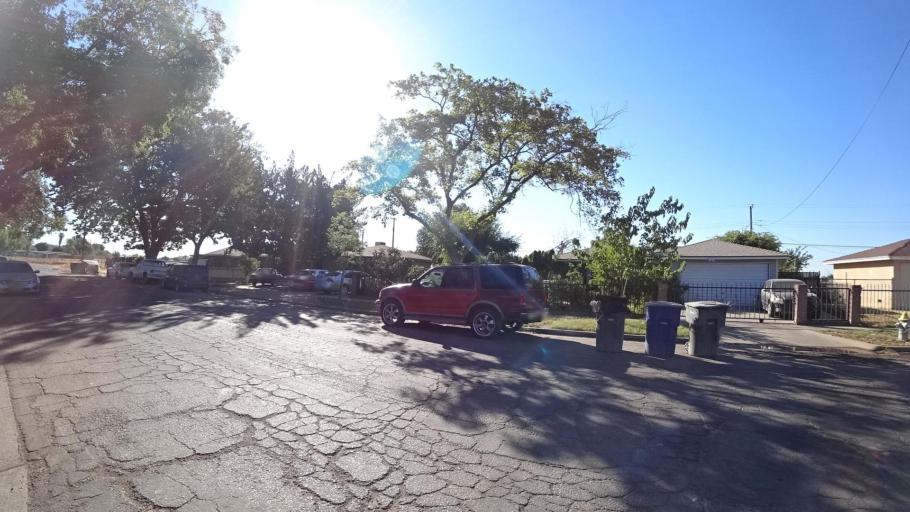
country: US
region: California
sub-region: Fresno County
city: Fresno
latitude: 36.7019
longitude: -119.7960
